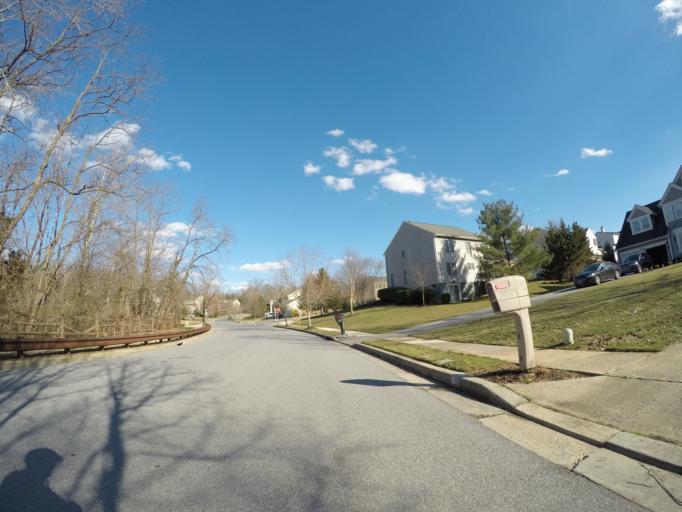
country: US
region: Maryland
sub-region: Howard County
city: Ellicott City
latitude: 39.2546
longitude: -76.8050
